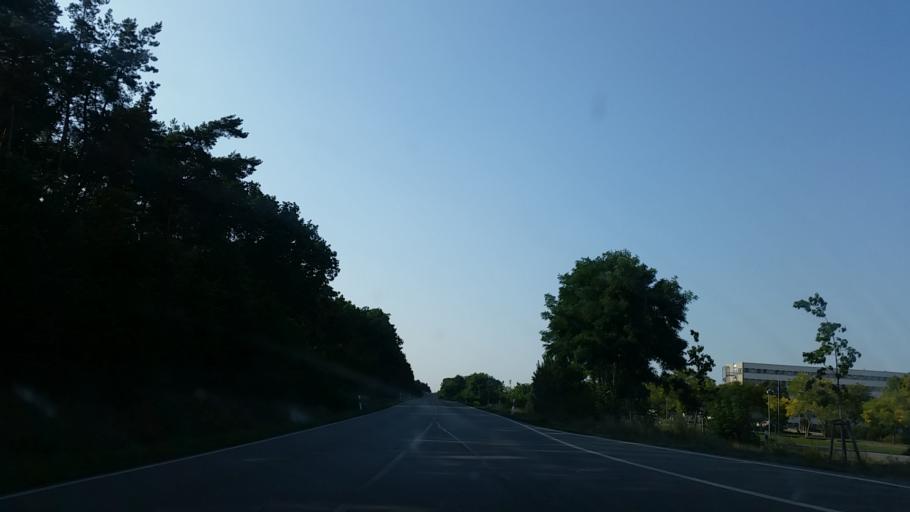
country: DE
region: Brandenburg
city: Meyenburg
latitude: 53.0869
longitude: 14.2273
